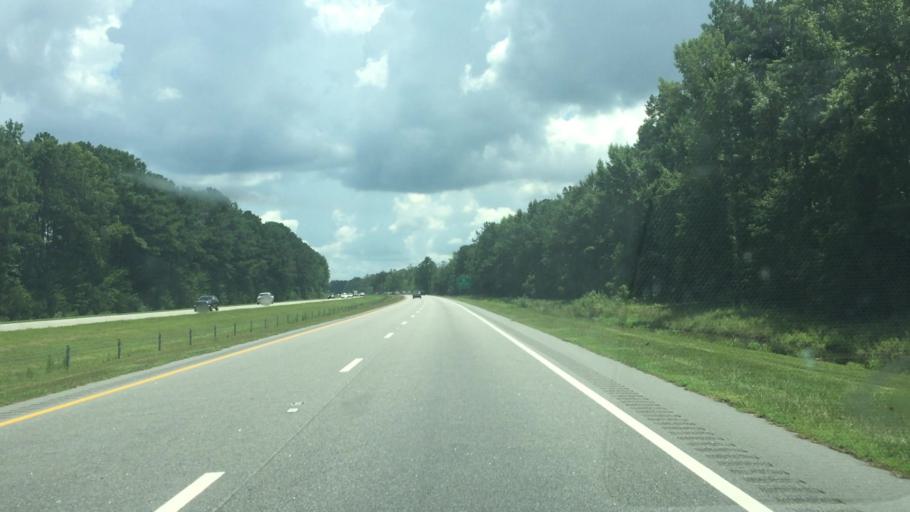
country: US
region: North Carolina
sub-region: Columbus County
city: Chadbourn
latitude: 34.4049
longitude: -78.9217
